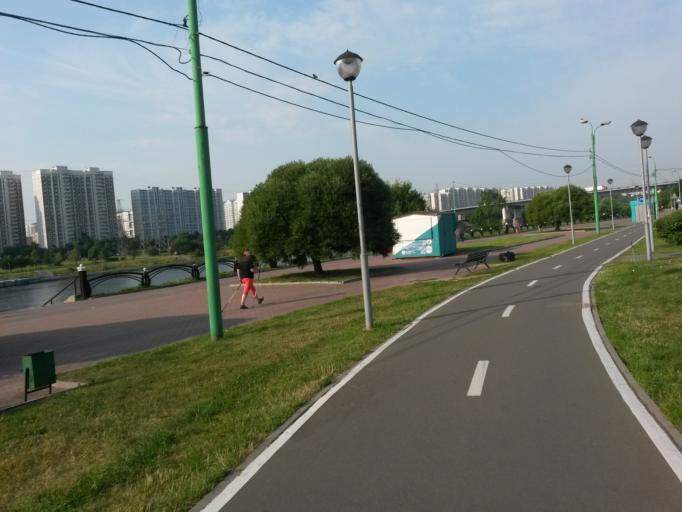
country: RU
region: Moscow
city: Brateyevo
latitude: 55.6431
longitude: 37.7537
